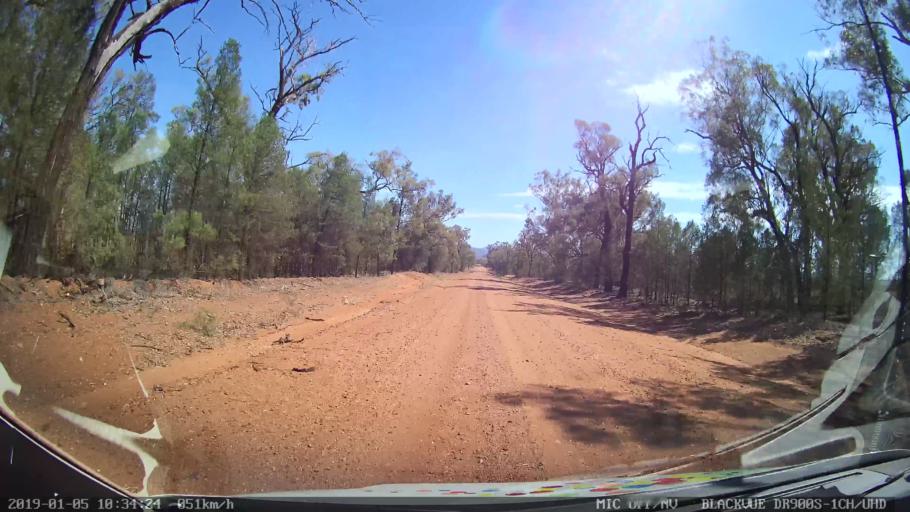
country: AU
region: New South Wales
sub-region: Gilgandra
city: Gilgandra
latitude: -31.4987
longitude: 148.9291
